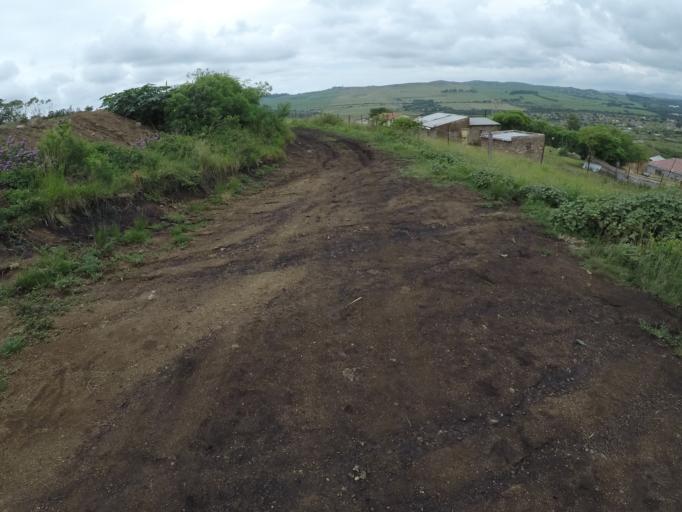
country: ZA
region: KwaZulu-Natal
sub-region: uThungulu District Municipality
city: Empangeni
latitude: -28.7064
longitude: 31.8515
